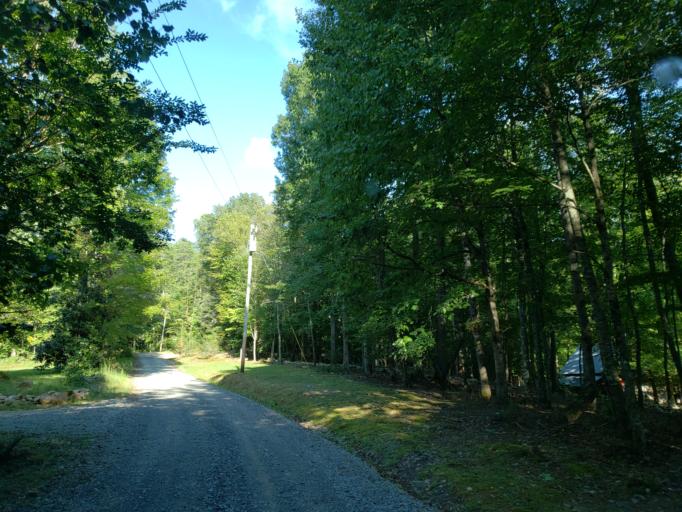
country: US
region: Georgia
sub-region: Fannin County
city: Blue Ridge
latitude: 34.6752
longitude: -84.2641
